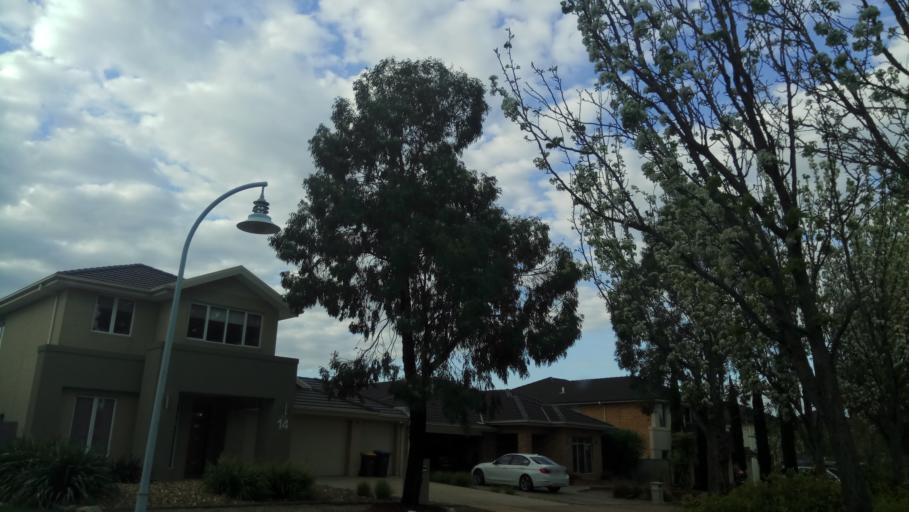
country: AU
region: Victoria
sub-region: Hobsons Bay
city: Altona Meadows
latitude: -37.8942
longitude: 144.7752
